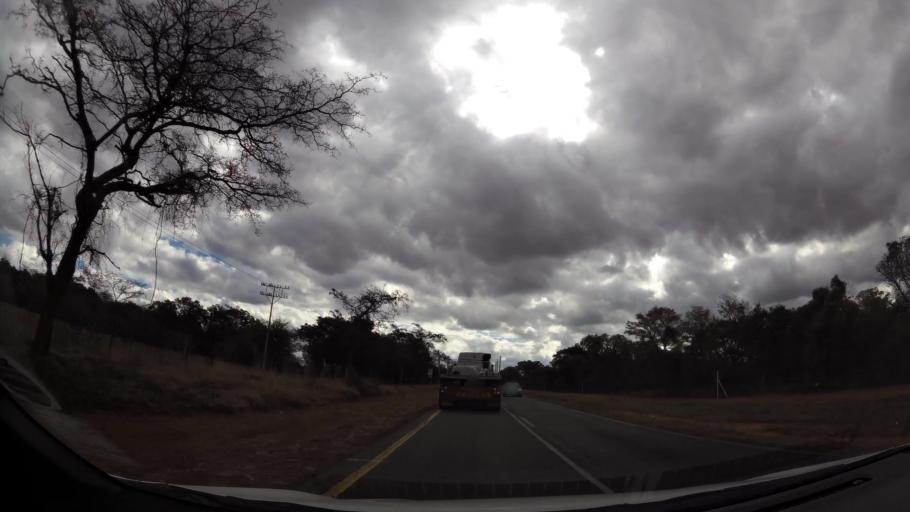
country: ZA
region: Limpopo
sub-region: Waterberg District Municipality
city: Modimolle
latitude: -24.7341
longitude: 28.4331
